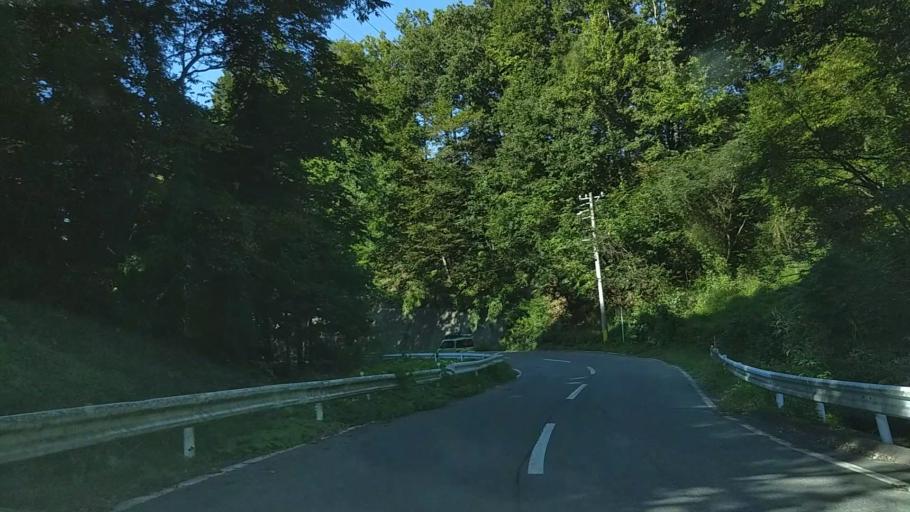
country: JP
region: Nagano
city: Nagano-shi
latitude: 36.6023
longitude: 138.0940
